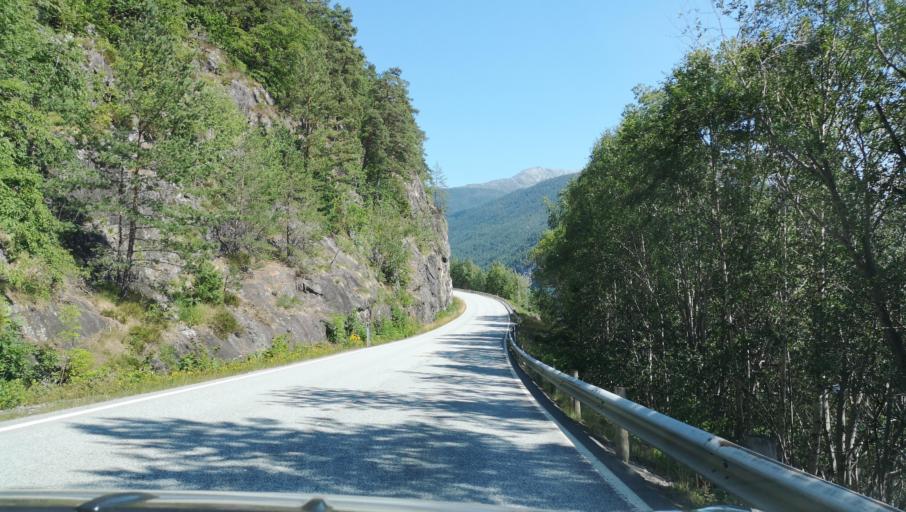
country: NO
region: Hordaland
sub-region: Ulvik
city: Ulvik
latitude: 60.4893
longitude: 6.8885
